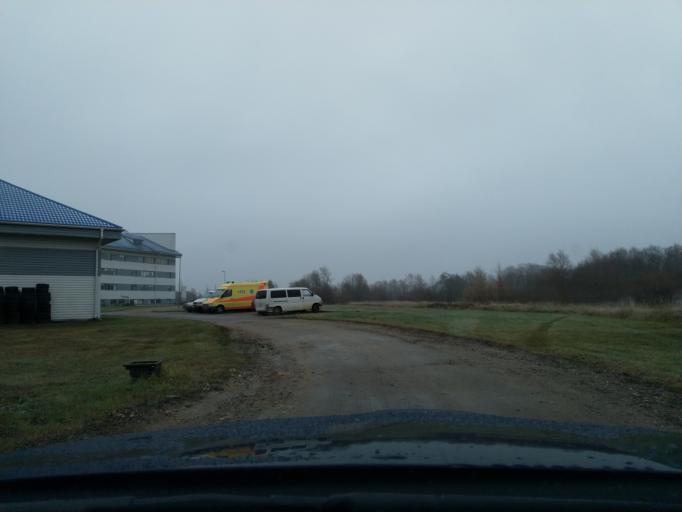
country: LV
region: Kuldigas Rajons
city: Kuldiga
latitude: 56.9600
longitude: 21.9534
